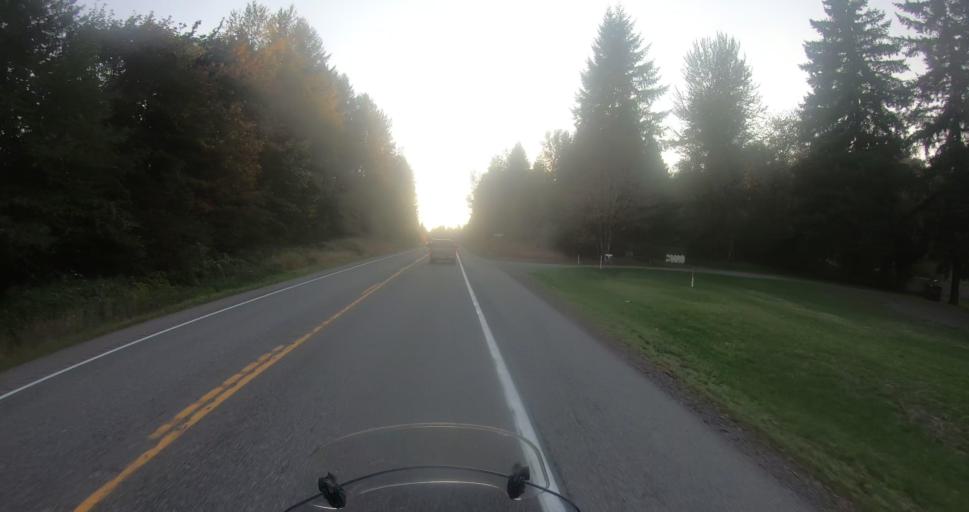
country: US
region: Washington
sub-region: Lewis County
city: Morton
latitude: 46.5156
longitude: -122.1672
